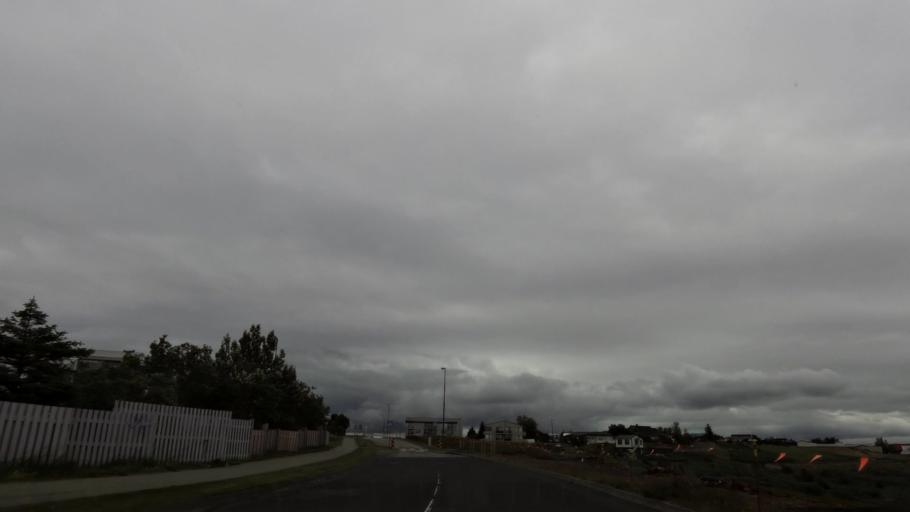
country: IS
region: Capital Region
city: Hafnarfjoerdur
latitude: 64.0544
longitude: -21.9788
